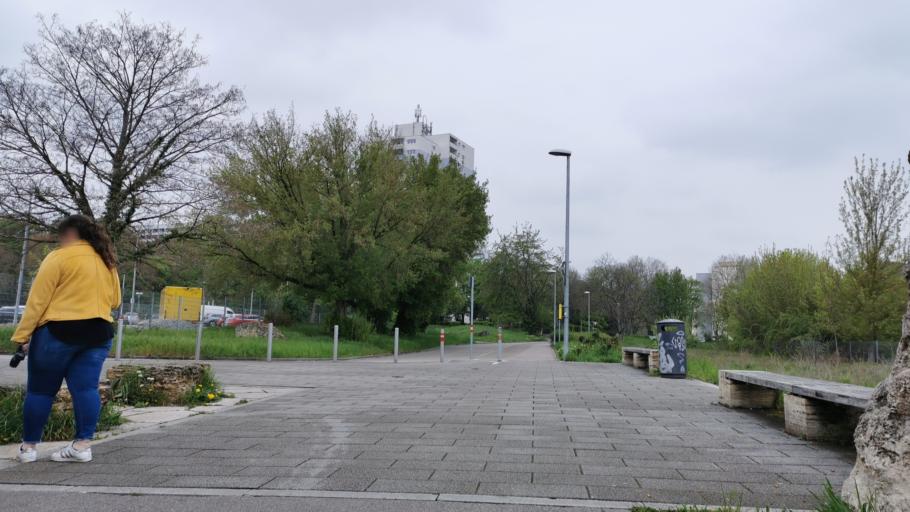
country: DE
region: Baden-Wuerttemberg
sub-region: Regierungsbezirk Stuttgart
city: Stuttgart Muehlhausen
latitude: 48.8186
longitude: 9.2144
